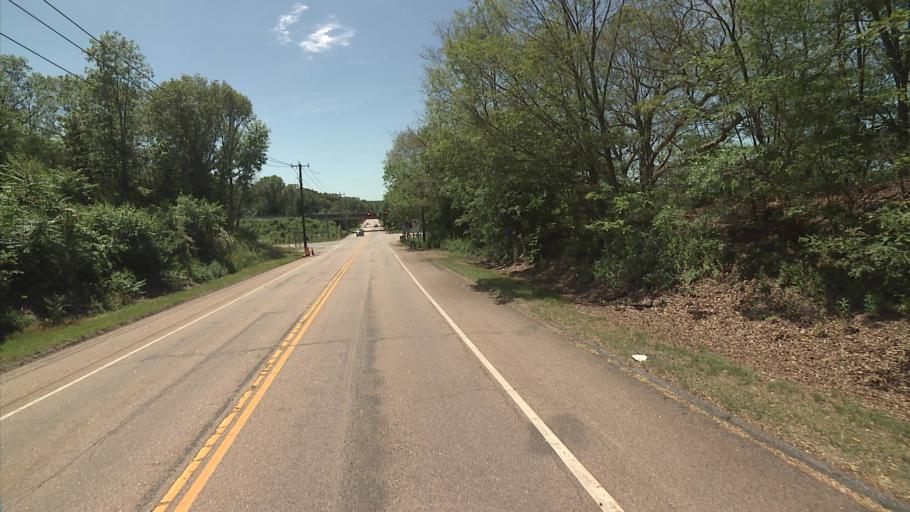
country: US
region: Connecticut
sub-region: New London County
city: Pawcatuck
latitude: 41.4220
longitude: -71.8447
